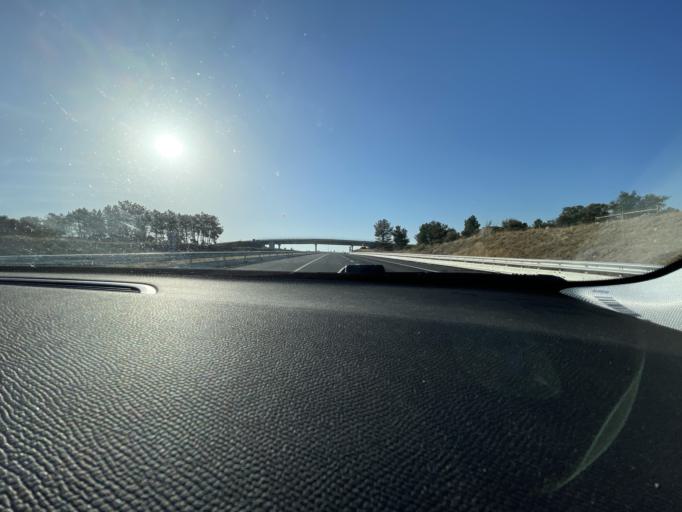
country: ES
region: Castille and Leon
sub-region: Provincia de Salamanca
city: Fuentes de Onoro
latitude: 40.6148
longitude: -6.8239
